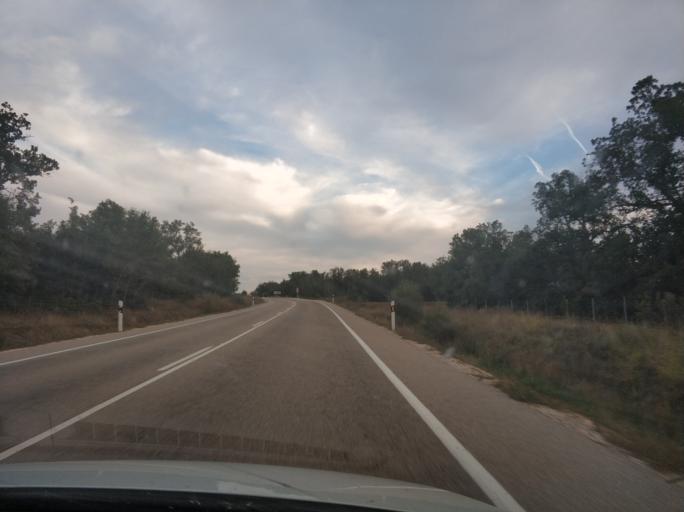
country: ES
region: Castille and Leon
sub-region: Provincia de Burgos
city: Pinilla de los Barruecos
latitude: 41.9301
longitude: -3.2824
